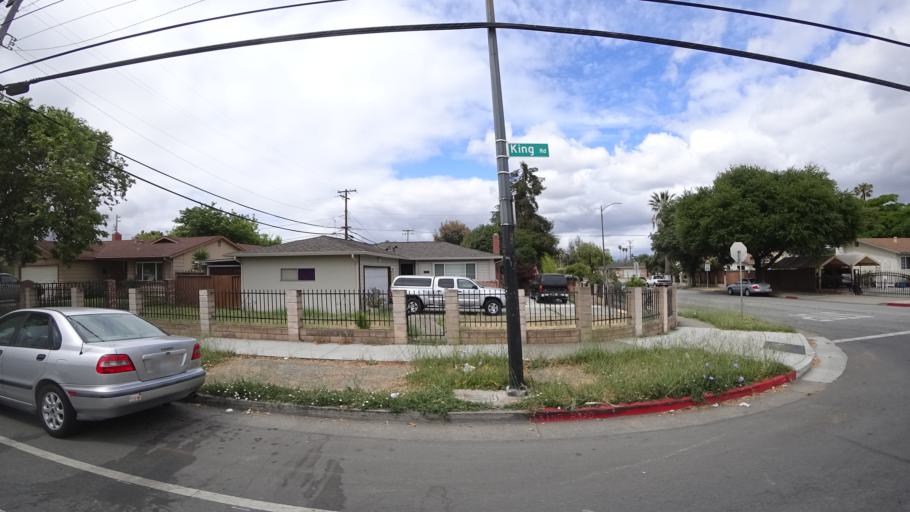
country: US
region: California
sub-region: Santa Clara County
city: Alum Rock
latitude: 37.3267
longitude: -121.8303
